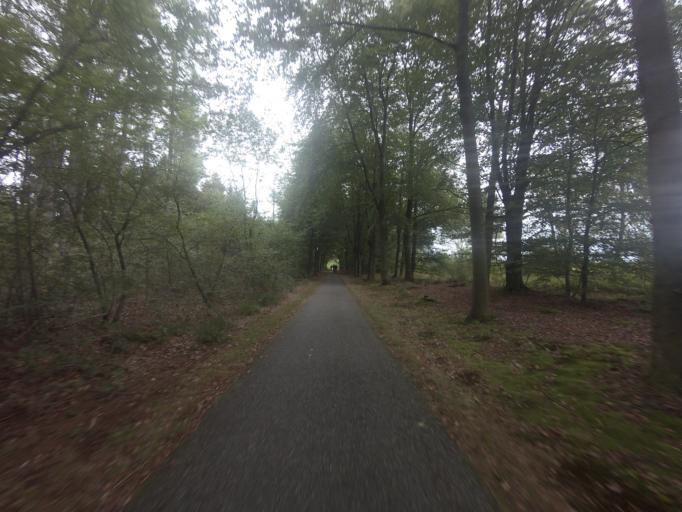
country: NL
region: Drenthe
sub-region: Gemeente Westerveld
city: Dwingeloo
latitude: 52.9038
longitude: 6.3017
